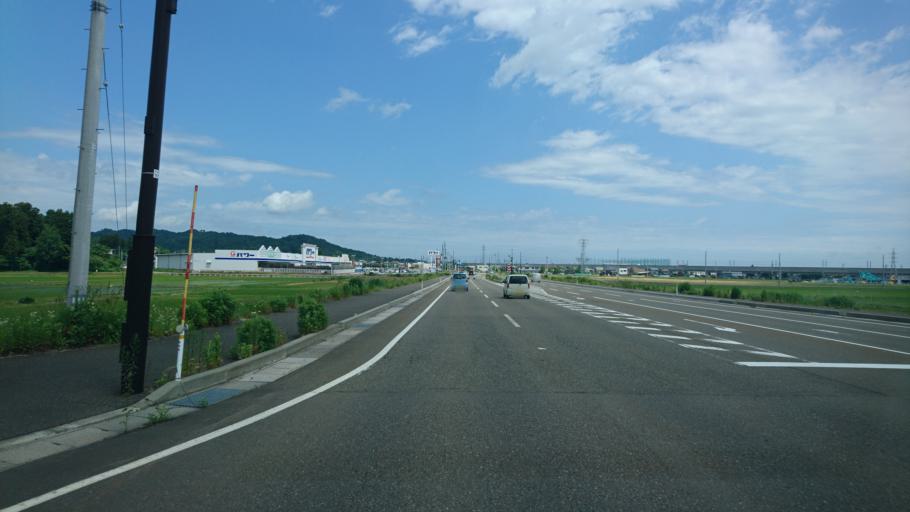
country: JP
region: Niigata
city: Joetsu
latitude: 37.0865
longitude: 138.2336
